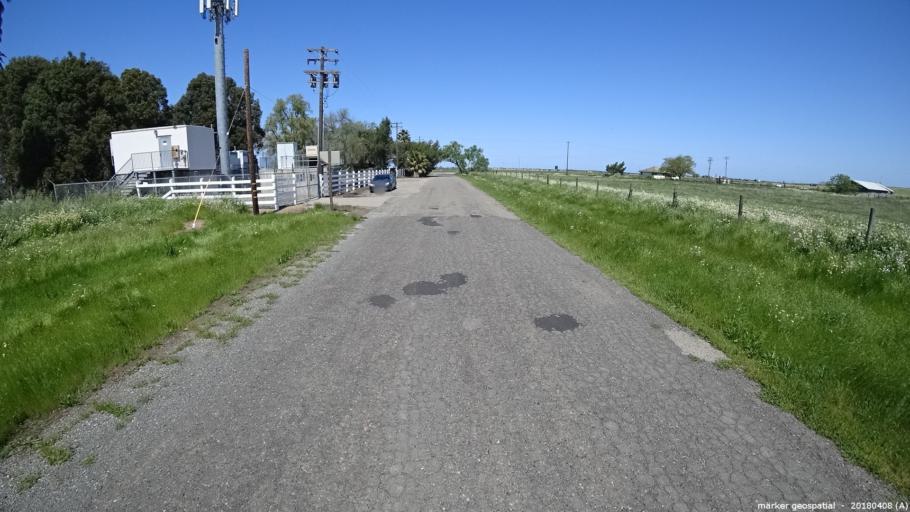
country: US
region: California
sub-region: Sacramento County
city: Laguna
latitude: 38.3736
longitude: -121.4821
